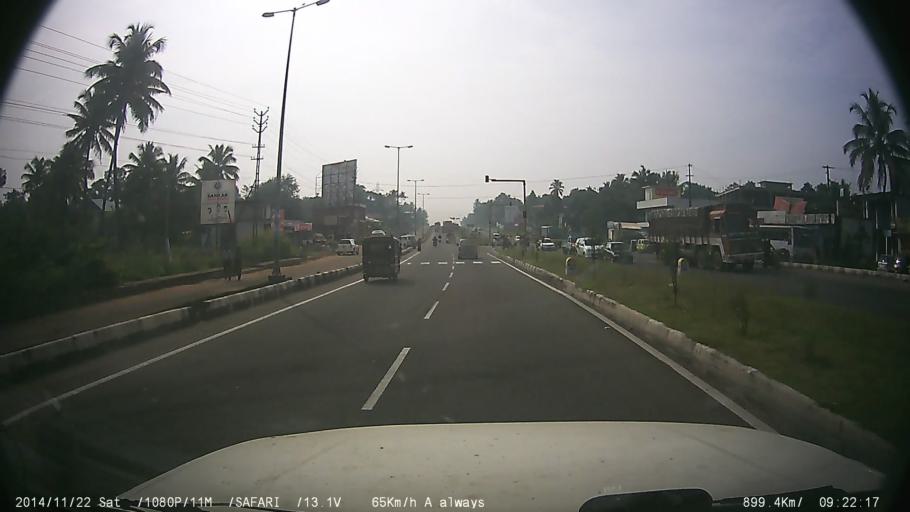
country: IN
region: Kerala
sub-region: Ernakulam
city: Angamali
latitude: 10.2178
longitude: 76.3776
